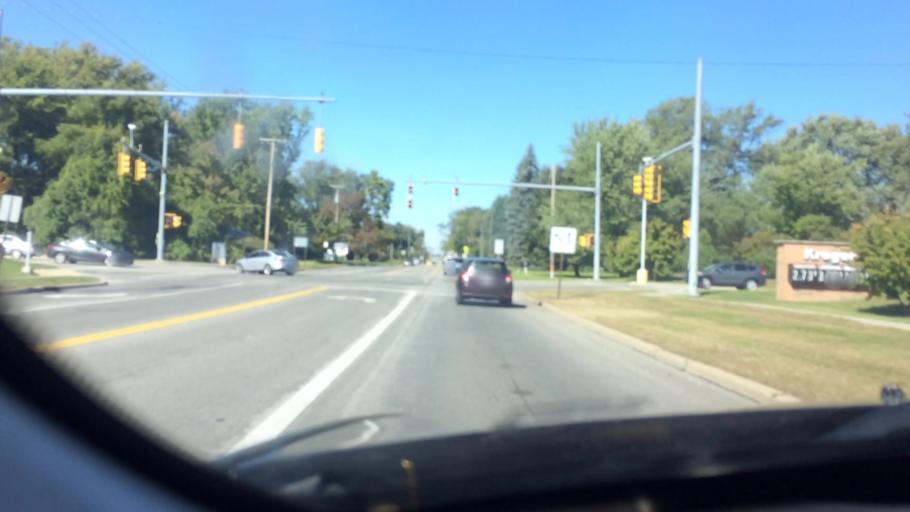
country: US
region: Ohio
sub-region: Lucas County
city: Ottawa Hills
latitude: 41.6628
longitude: -83.6825
